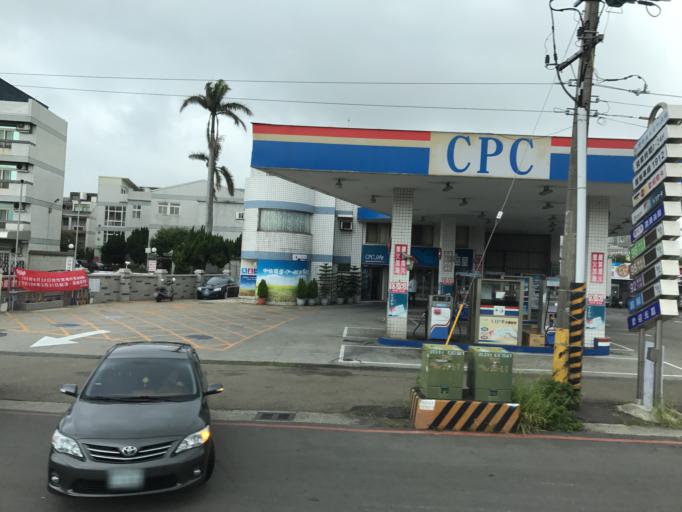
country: TW
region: Taiwan
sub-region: Hsinchu
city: Hsinchu
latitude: 24.8182
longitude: 120.9555
